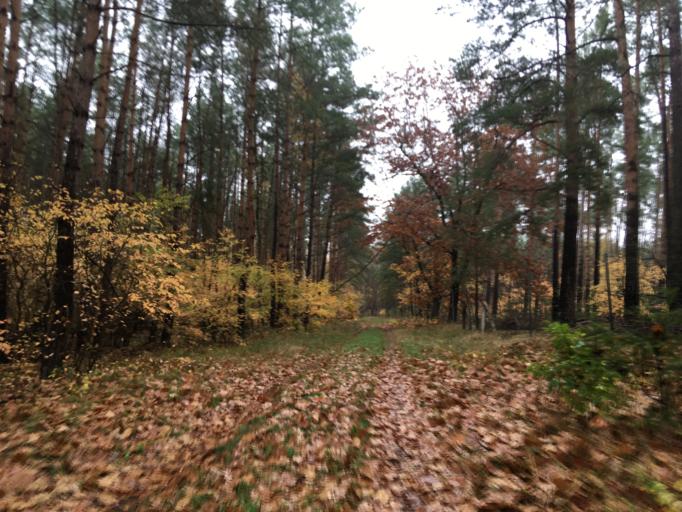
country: DE
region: Brandenburg
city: Briesen
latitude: 52.2591
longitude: 14.2946
